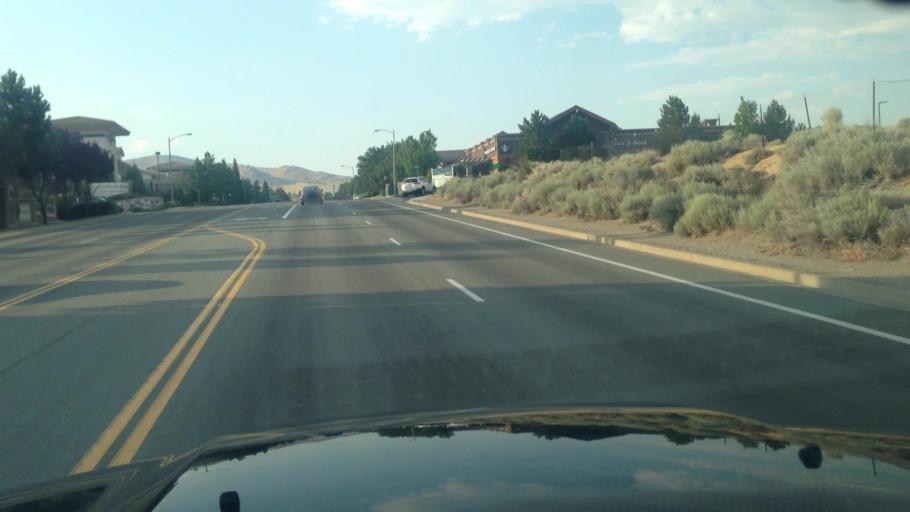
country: US
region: Nevada
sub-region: Washoe County
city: Mogul
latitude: 39.5262
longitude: -119.8822
